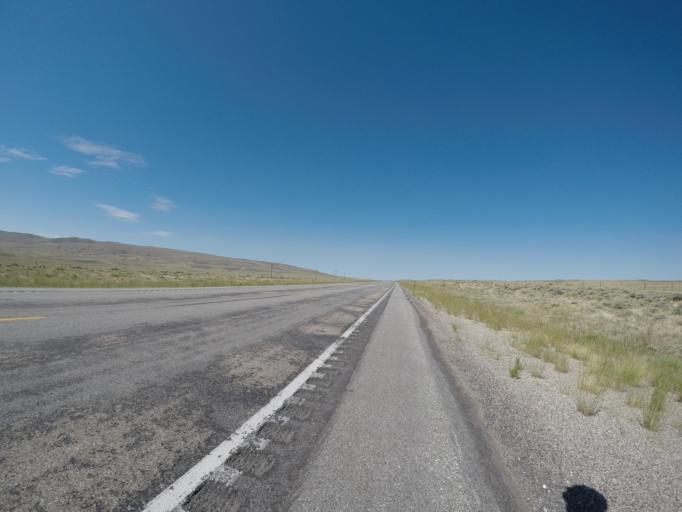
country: US
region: Wyoming
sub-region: Carbon County
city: Saratoga
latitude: 41.8021
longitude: -106.7060
